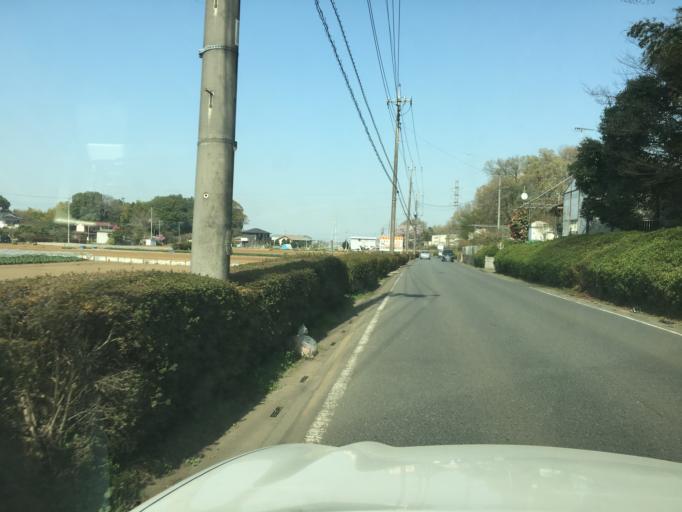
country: JP
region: Saitama
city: Kamifukuoka
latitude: 35.8623
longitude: 139.4897
